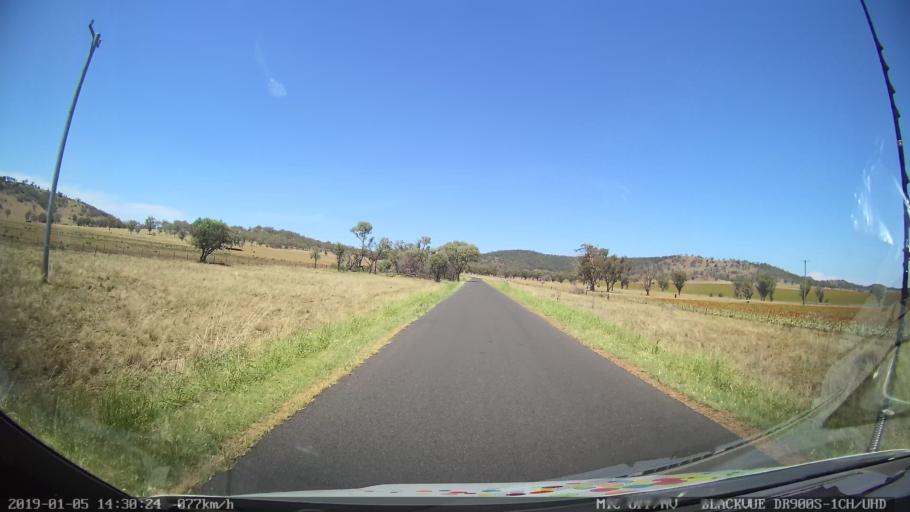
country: AU
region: New South Wales
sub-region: Tamworth Municipality
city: Phillip
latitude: -31.2279
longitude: 150.5924
